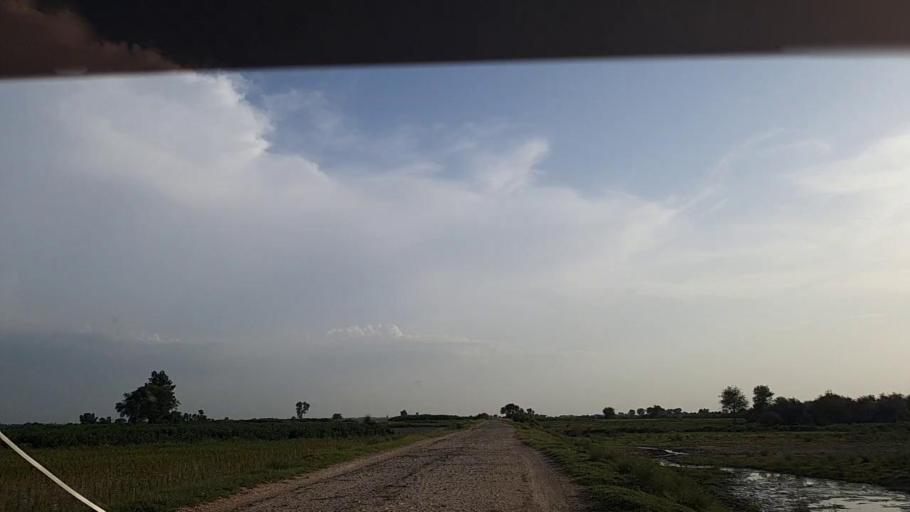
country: PK
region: Sindh
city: Khanpur
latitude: 27.8064
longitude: 69.3180
